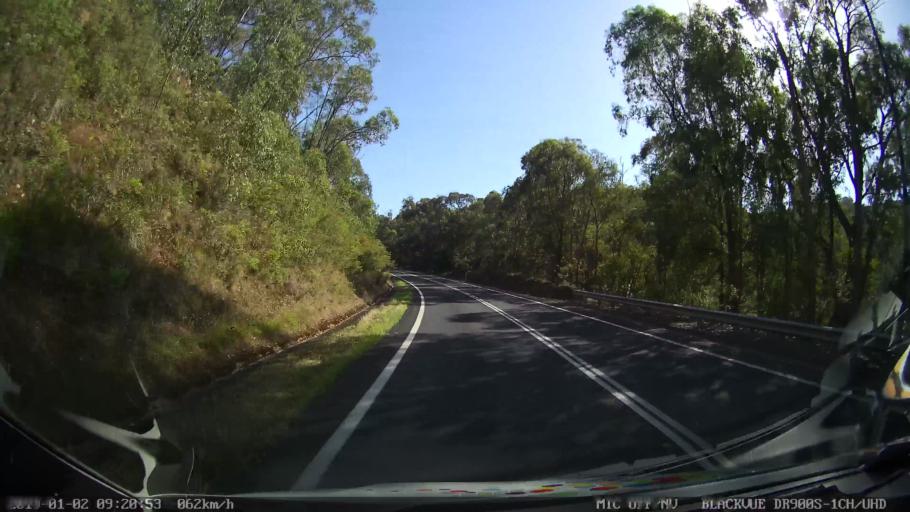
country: AU
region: New South Wales
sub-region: Tumut Shire
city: Tumut
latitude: -35.4114
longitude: 148.2885
